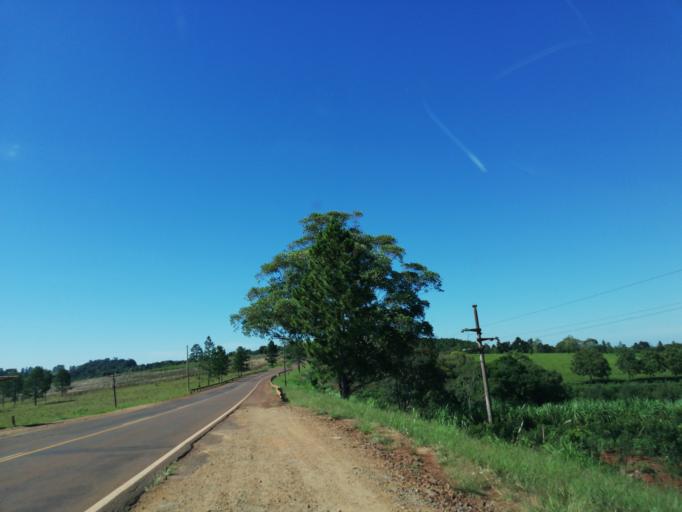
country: AR
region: Misiones
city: Dos de Mayo
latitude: -27.0773
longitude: -54.4028
